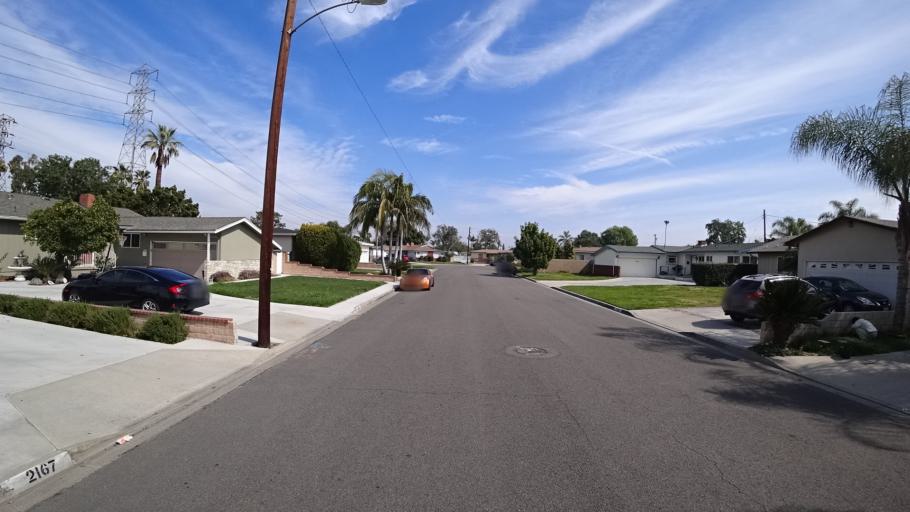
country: US
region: California
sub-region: Orange County
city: Stanton
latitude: 33.8063
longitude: -117.9580
